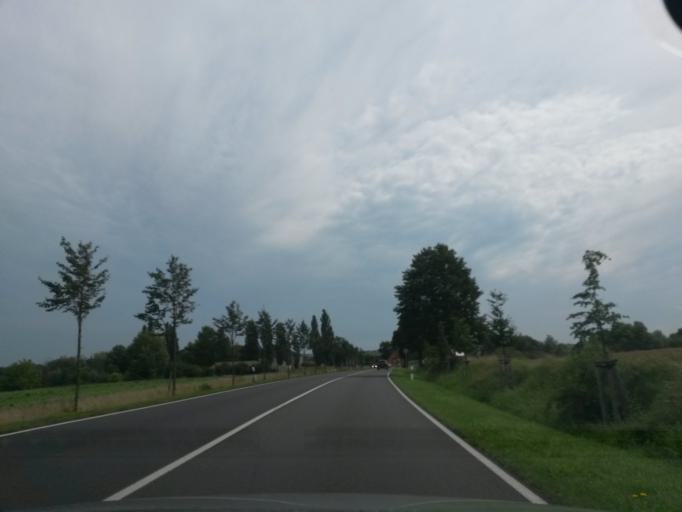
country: DE
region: Brandenburg
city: Schoneberg
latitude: 53.0315
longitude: 14.1612
